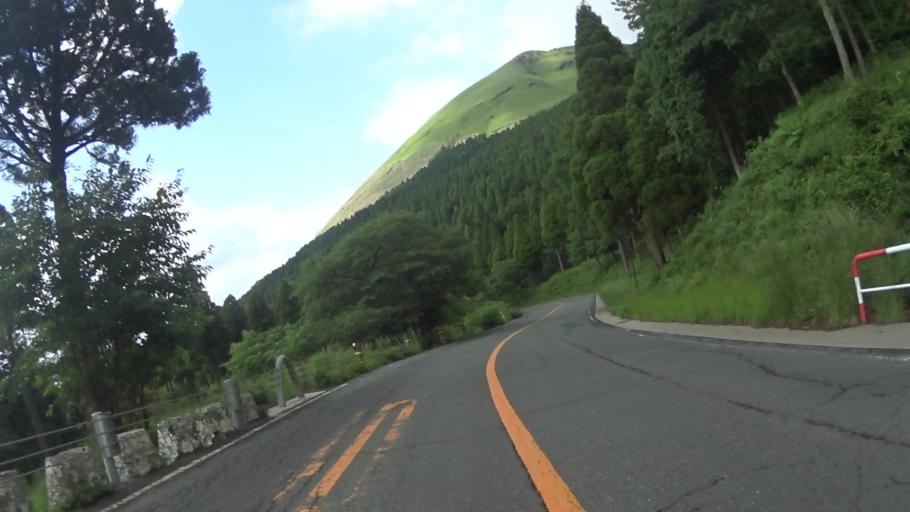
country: JP
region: Kumamoto
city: Aso
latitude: 32.8912
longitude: 131.0500
